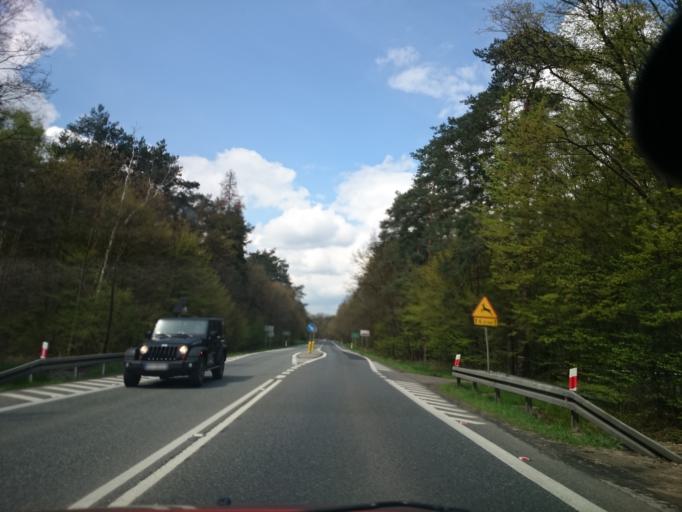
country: PL
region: Opole Voivodeship
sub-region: Powiat opolski
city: Tarnow Opolski
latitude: 50.6125
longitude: 18.0679
